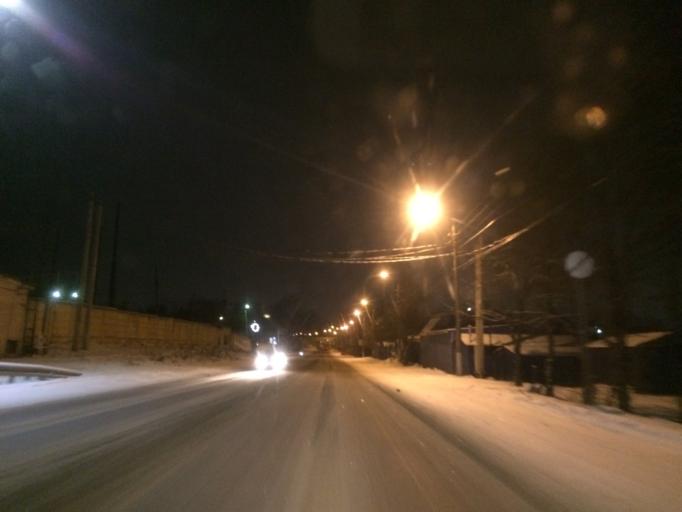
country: RU
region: Tula
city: Tula
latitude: 54.2202
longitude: 37.6491
